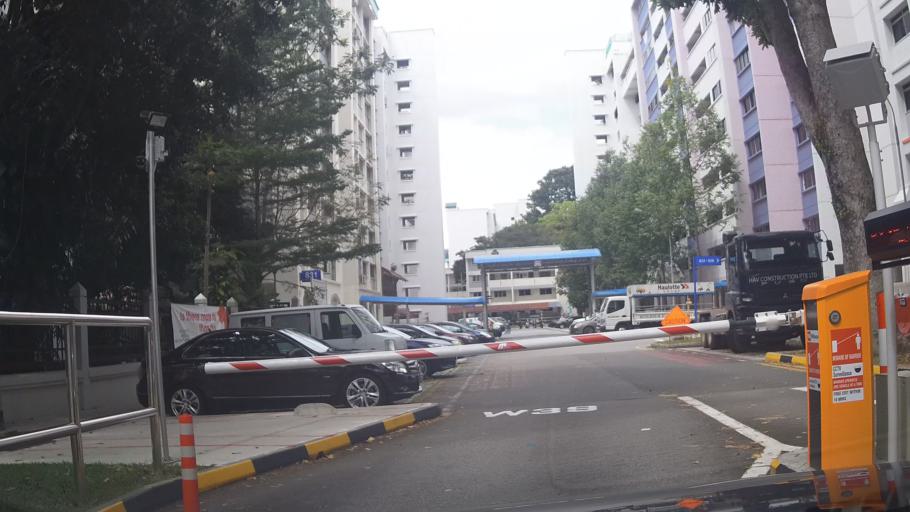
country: MY
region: Johor
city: Johor Bahru
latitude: 1.4400
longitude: 103.7919
